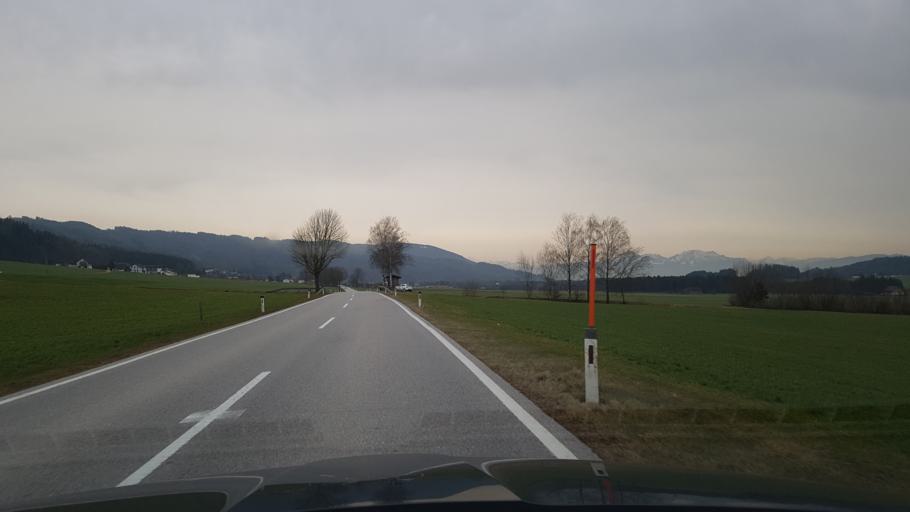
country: AT
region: Salzburg
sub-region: Politischer Bezirk Salzburg-Umgebung
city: Nussdorf am Haunsberg
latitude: 47.9746
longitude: 13.0091
